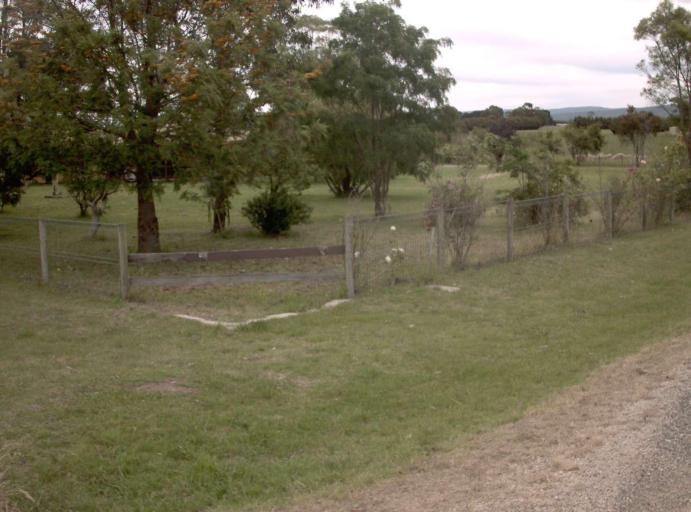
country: AU
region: Victoria
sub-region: East Gippsland
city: Bairnsdale
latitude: -37.8705
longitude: 147.5612
